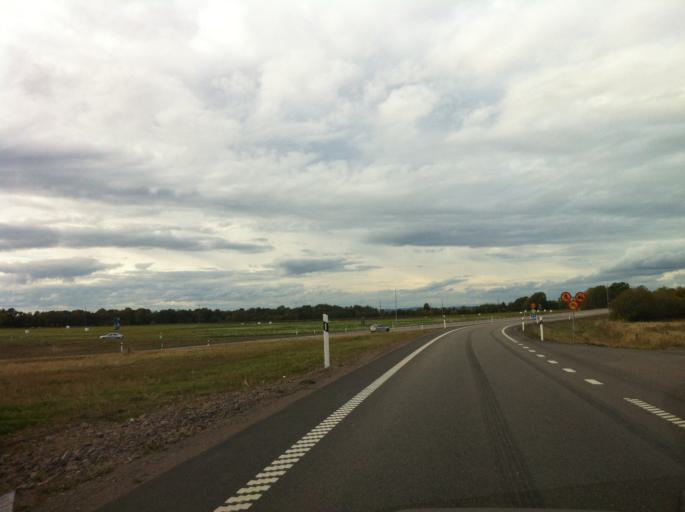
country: SE
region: OEstergoetland
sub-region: Motala Kommun
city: Motala
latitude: 58.5083
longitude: 15.0274
